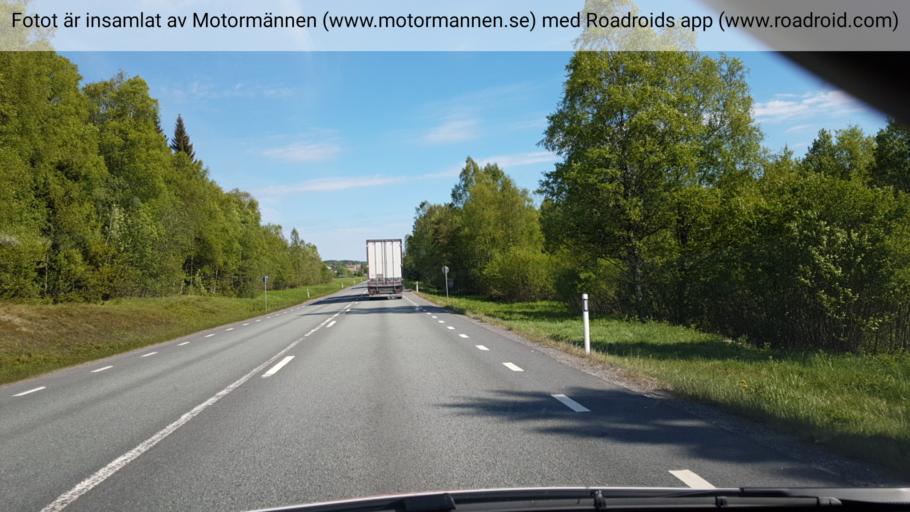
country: SE
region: Vaesterbotten
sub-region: Skelleftea Kommun
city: Burea
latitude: 64.3658
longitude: 21.2993
